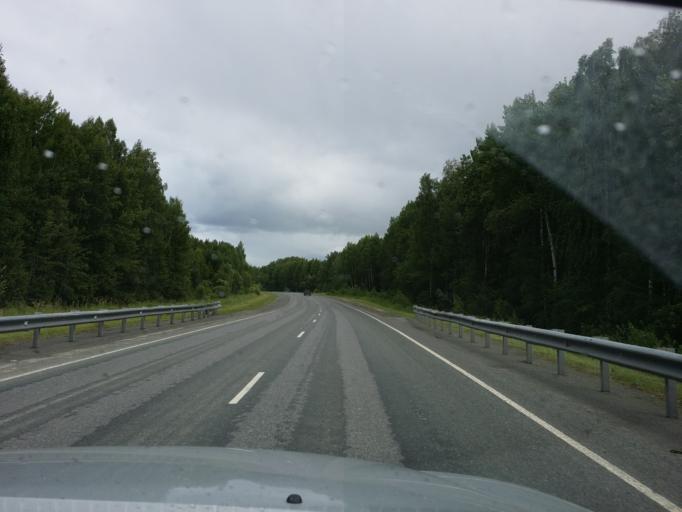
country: RU
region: Tjumen
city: Abalak
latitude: 58.4811
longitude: 68.6301
